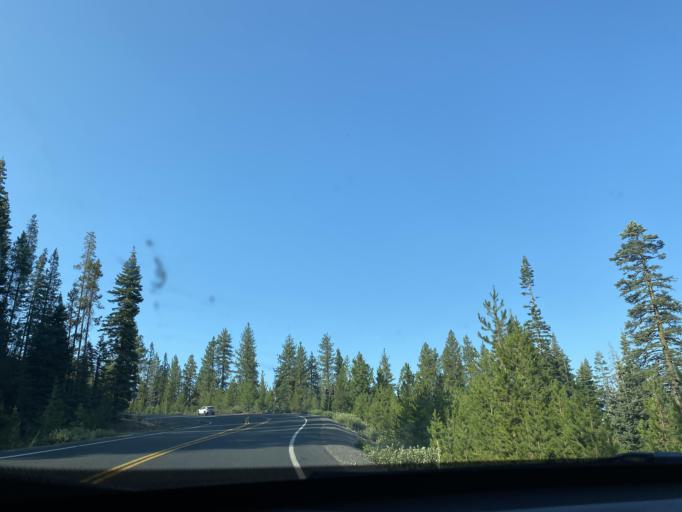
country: US
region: Oregon
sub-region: Deschutes County
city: La Pine
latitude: 43.7050
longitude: -121.3167
